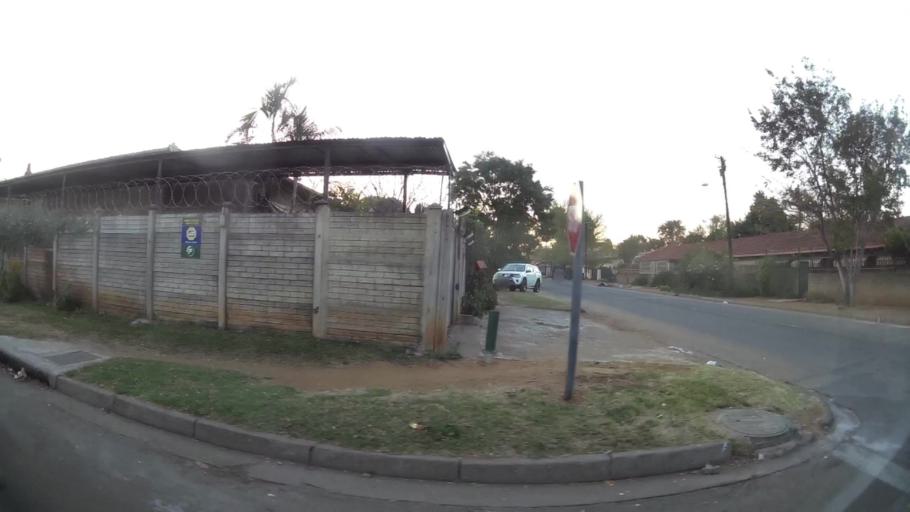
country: ZA
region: North-West
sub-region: Bojanala Platinum District Municipality
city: Rustenburg
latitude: -25.6664
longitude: 27.2481
